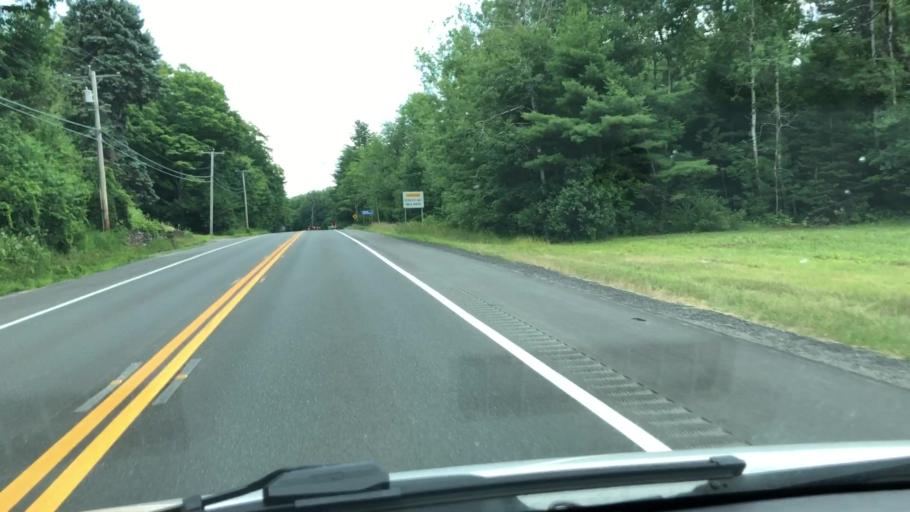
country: US
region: Massachusetts
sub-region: Hampshire County
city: Chesterfield
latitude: 42.4481
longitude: -72.8118
